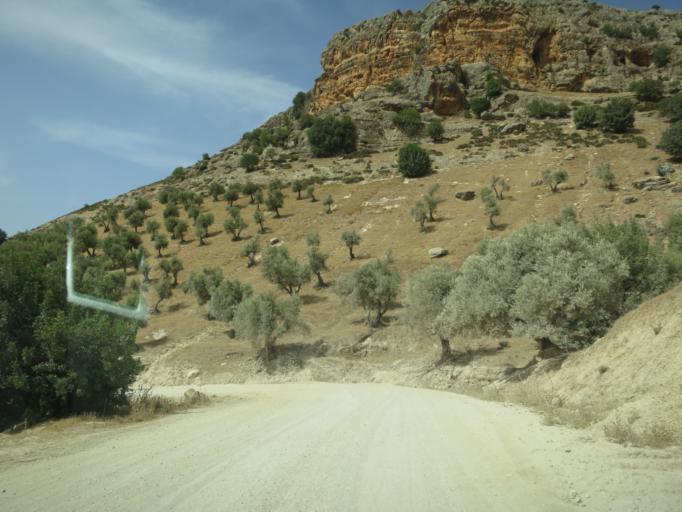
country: MA
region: Meknes-Tafilalet
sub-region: Meknes
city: Meknes
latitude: 34.0661
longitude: -5.5319
